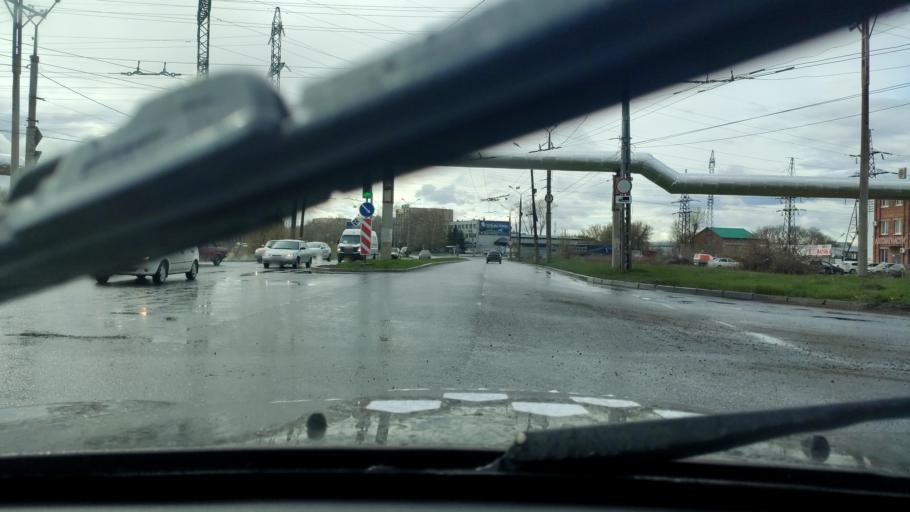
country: RU
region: Samara
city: Tol'yatti
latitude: 53.5329
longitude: 49.4400
